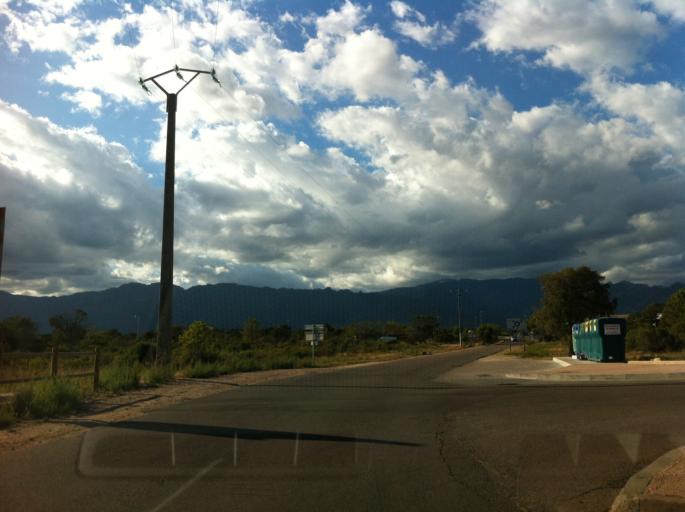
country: FR
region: Corsica
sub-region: Departement de la Corse-du-Sud
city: Porto-Vecchio
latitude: 41.6368
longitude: 9.3377
